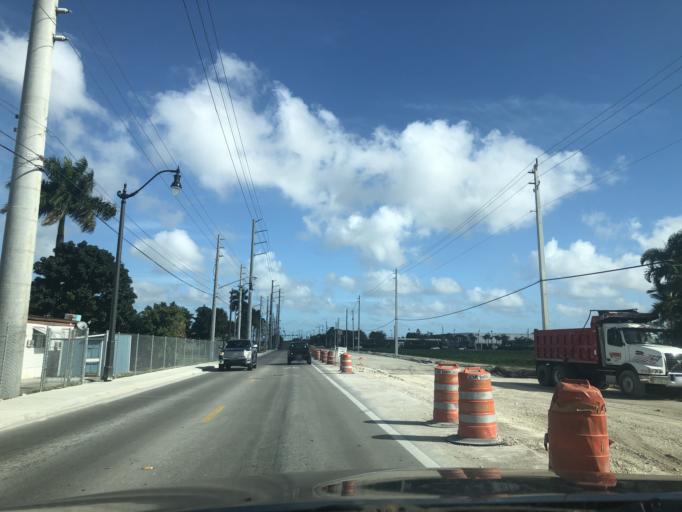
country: US
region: Florida
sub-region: Miami-Dade County
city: Homestead
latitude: 25.4625
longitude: -80.4719
